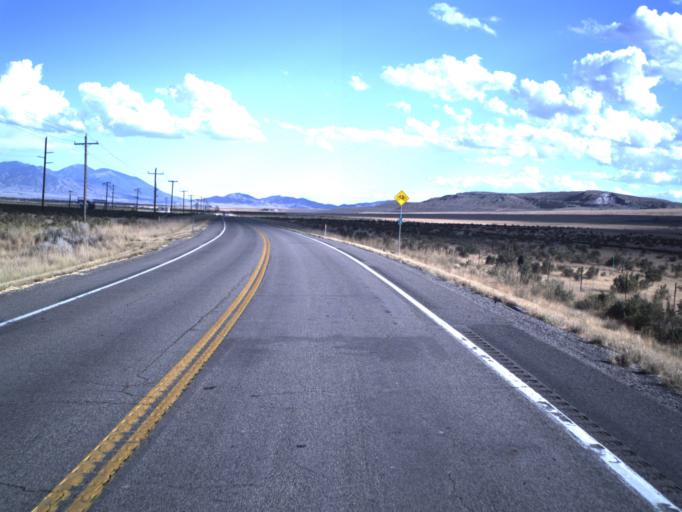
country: US
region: Utah
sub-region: Tooele County
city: Grantsville
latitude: 40.6749
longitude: -112.5500
